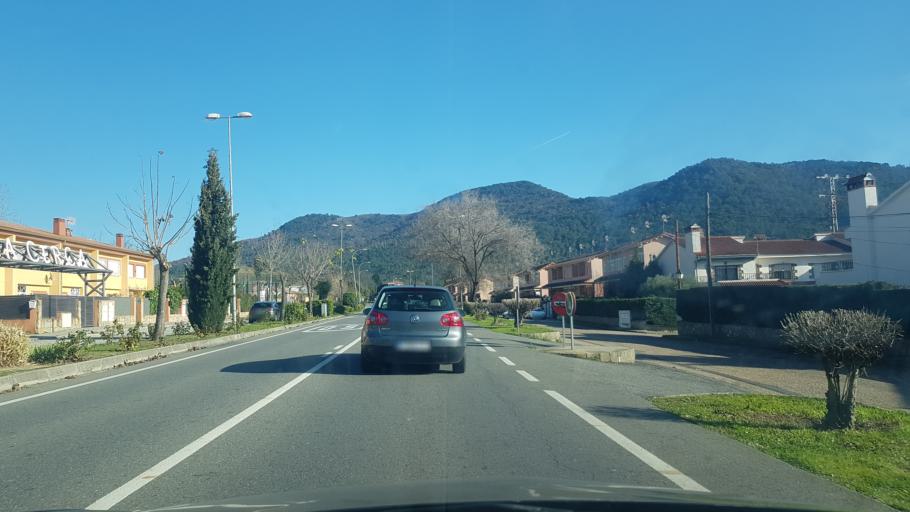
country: ES
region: Castille and Leon
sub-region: Provincia de Avila
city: Casillas
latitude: 40.3021
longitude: -4.5492
